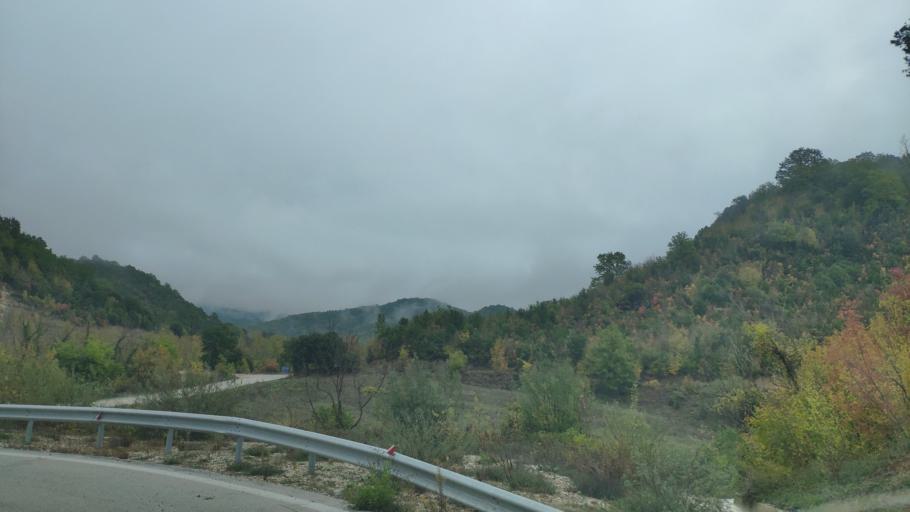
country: GR
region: Epirus
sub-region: Nomos Ioanninon
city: Pedini
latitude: 39.5172
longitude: 20.6907
